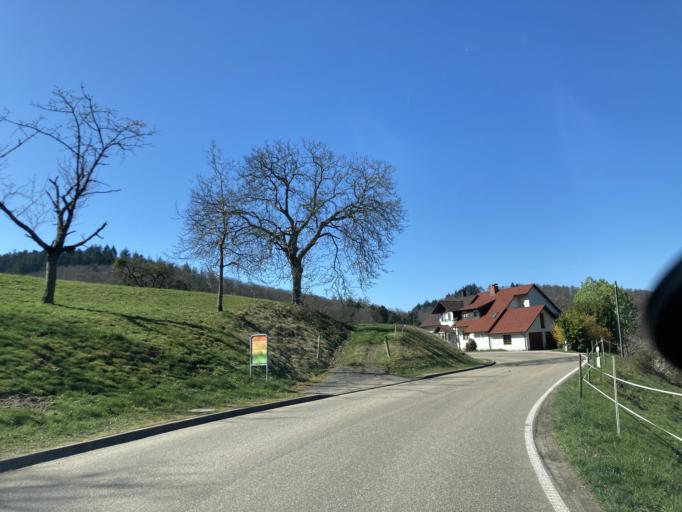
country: DE
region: Baden-Wuerttemberg
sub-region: Freiburg Region
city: Badenweiler
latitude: 47.7805
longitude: 7.6745
